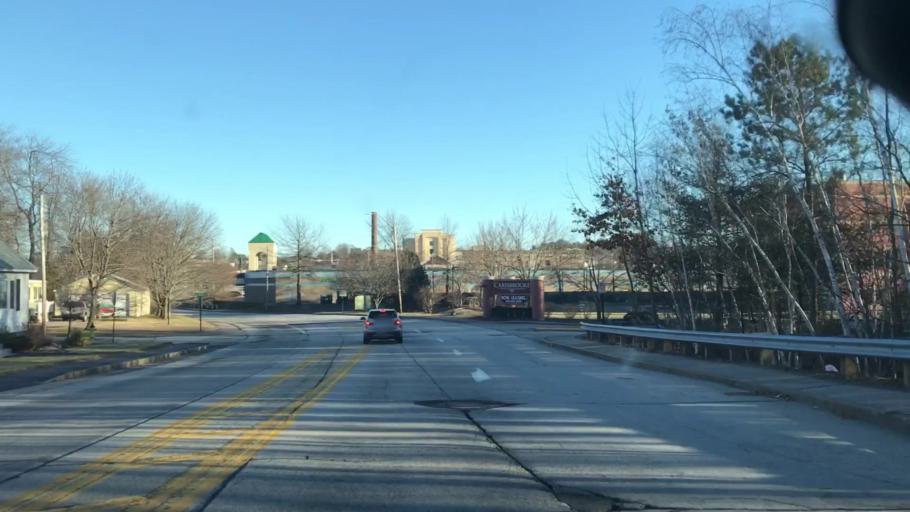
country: US
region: New Hampshire
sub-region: Hillsborough County
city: Manchester
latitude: 42.9757
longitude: -71.4780
